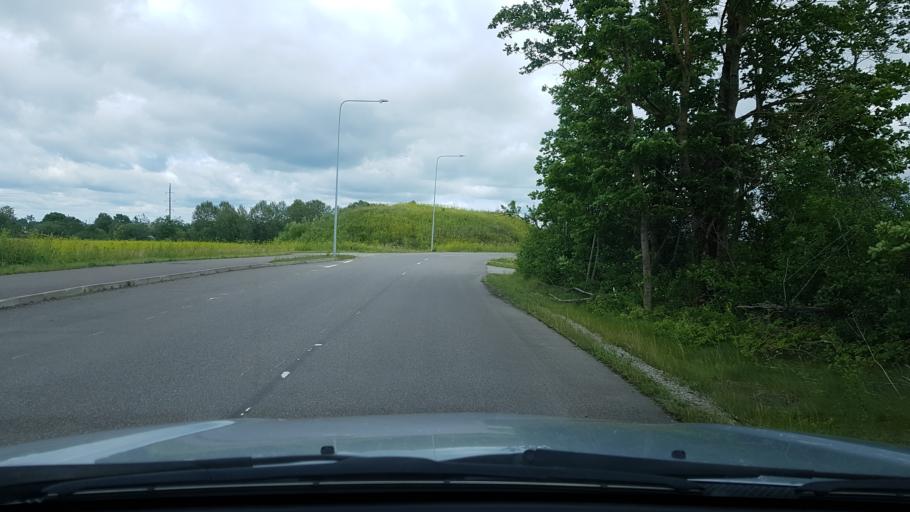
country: EE
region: Ida-Virumaa
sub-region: Narva linn
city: Narva
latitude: 59.3924
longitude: 28.1194
